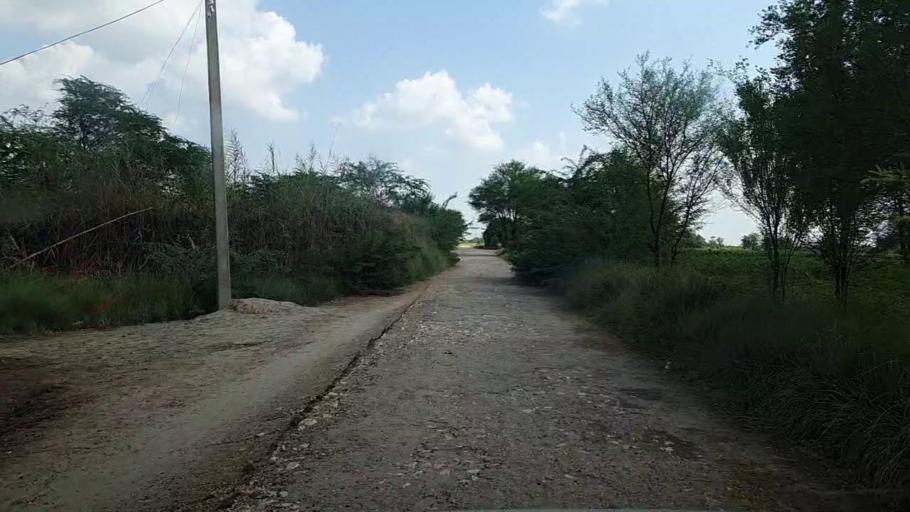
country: PK
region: Sindh
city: Kandiaro
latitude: 26.9905
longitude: 68.3053
